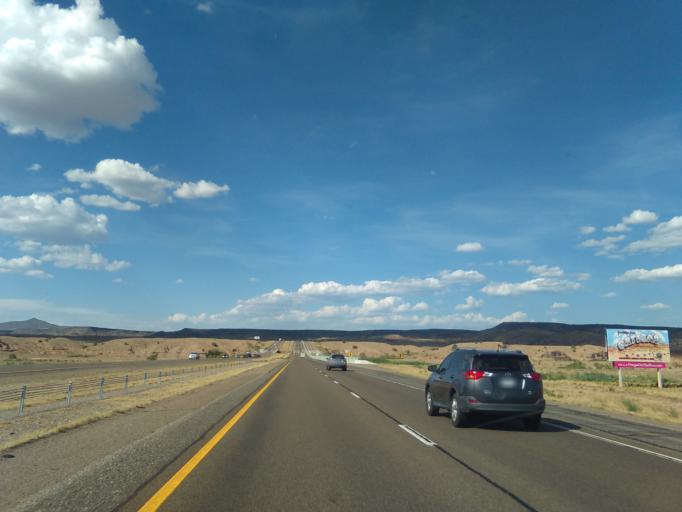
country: US
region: New Mexico
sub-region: Sandoval County
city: Santo Domingo Pueblo
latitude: 35.4968
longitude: -106.2541
